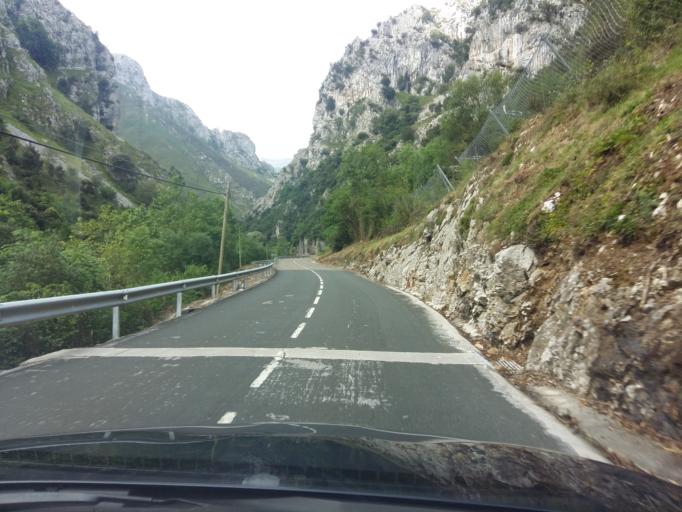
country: ES
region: Cantabria
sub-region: Provincia de Cantabria
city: Tresviso
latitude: 43.2877
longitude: -4.6246
